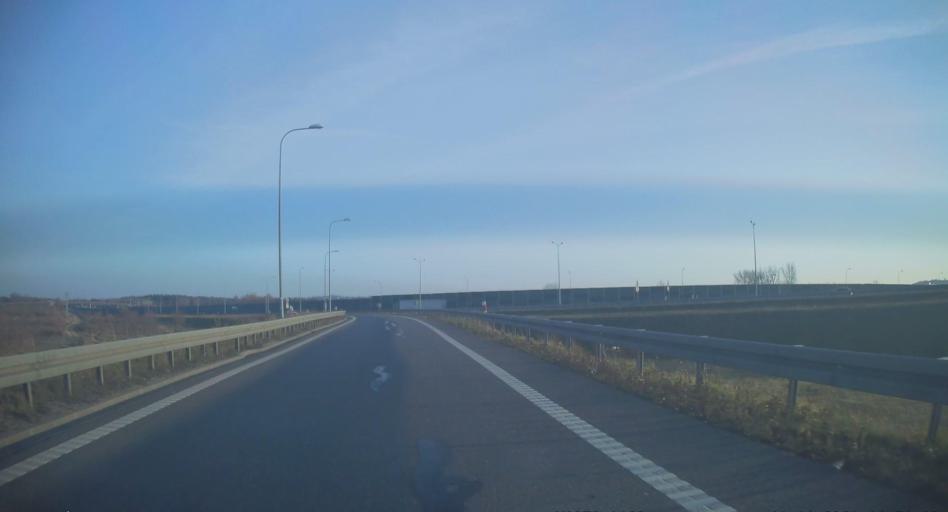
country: PL
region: Silesian Voivodeship
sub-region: Powiat tarnogorski
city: Ozarowice
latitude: 50.4543
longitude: 19.0585
